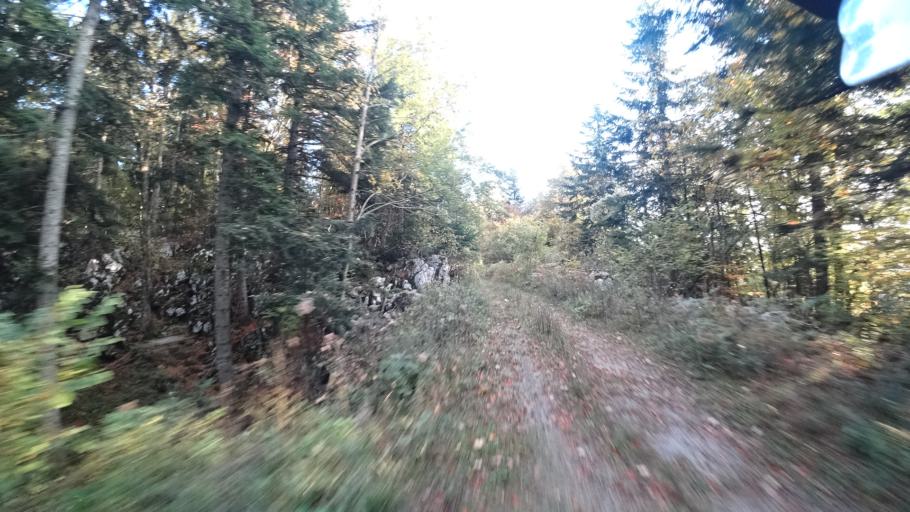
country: HR
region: Karlovacka
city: Plaski
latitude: 45.0287
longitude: 15.4307
